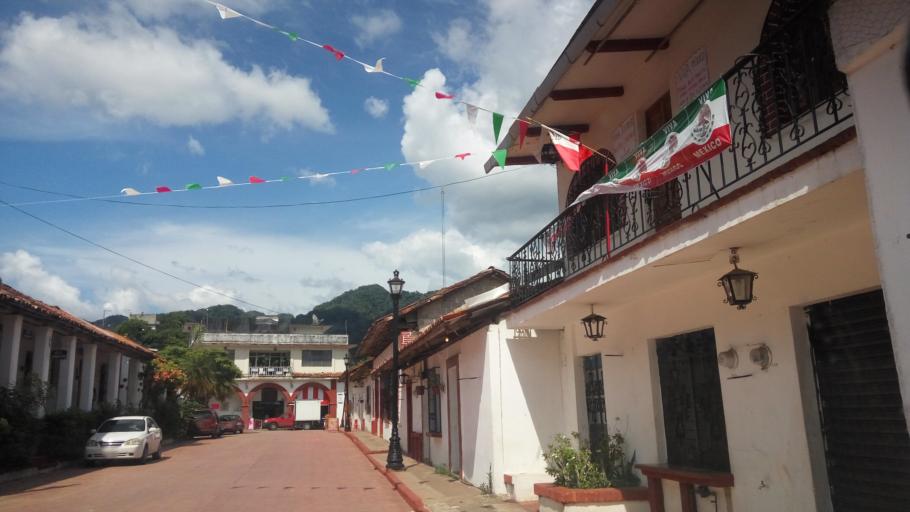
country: MX
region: Tabasco
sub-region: Tacotalpa
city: Libertad
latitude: 17.4602
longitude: -92.7785
